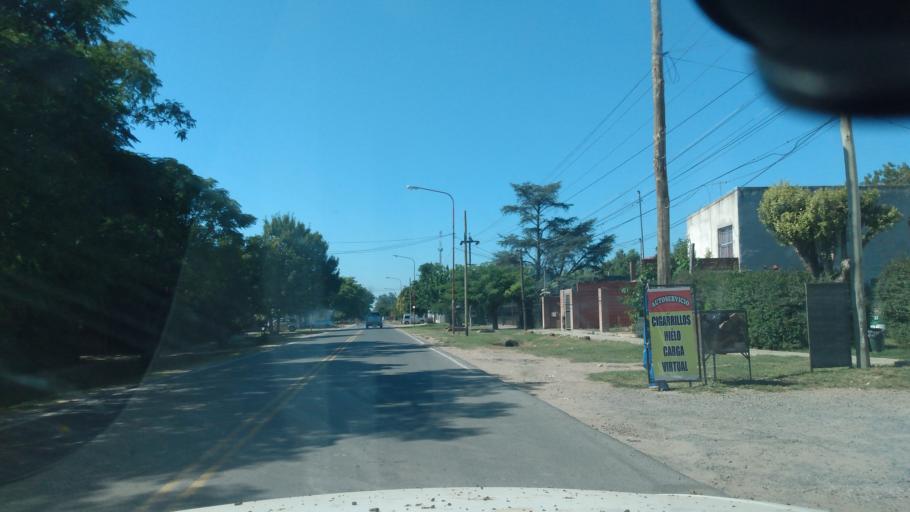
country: AR
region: Buenos Aires
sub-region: Partido de Lujan
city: Lujan
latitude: -34.4943
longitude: -59.0753
